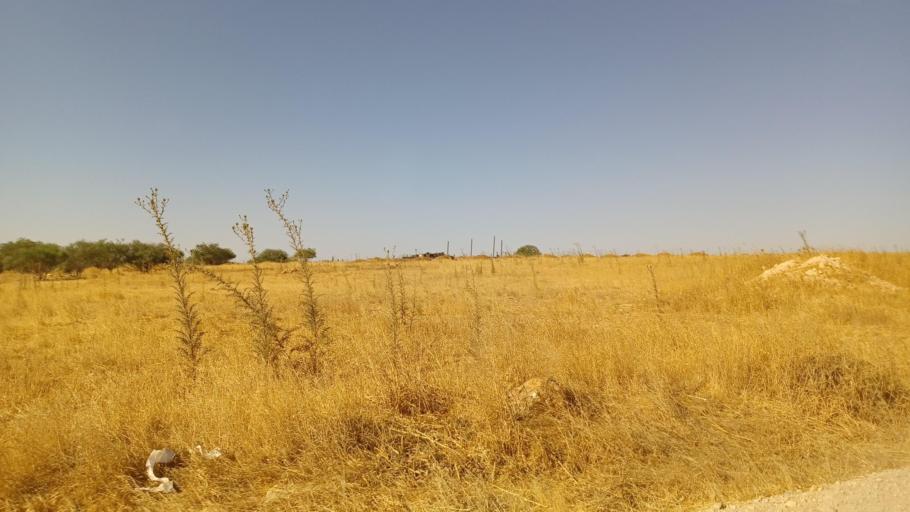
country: CY
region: Larnaka
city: Pergamos
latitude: 35.0524
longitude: 33.7018
